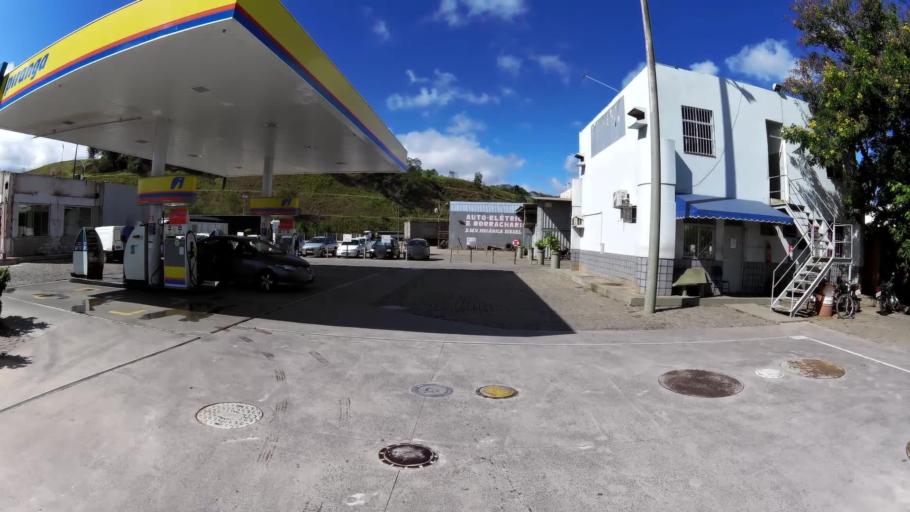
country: BR
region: Espirito Santo
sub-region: Serra
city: Serra
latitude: -20.2186
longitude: -40.2909
